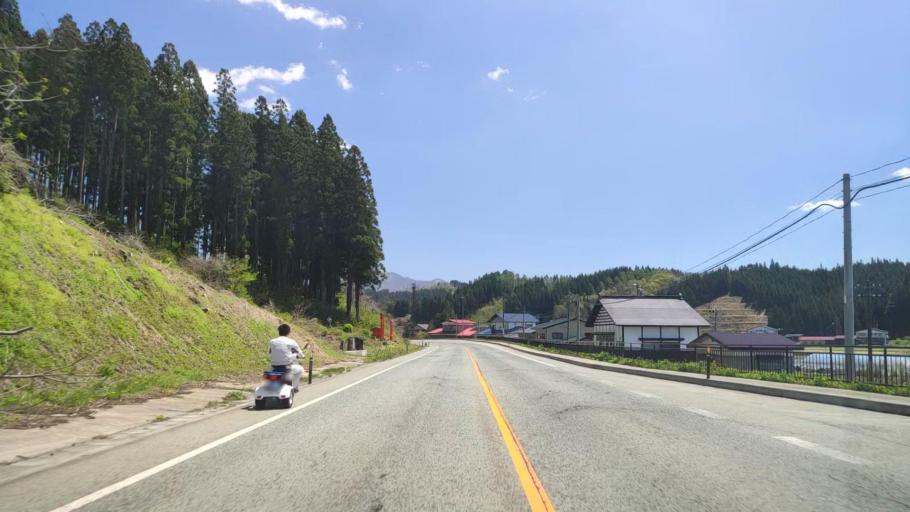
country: JP
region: Yamagata
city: Shinjo
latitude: 38.8899
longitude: 140.3251
